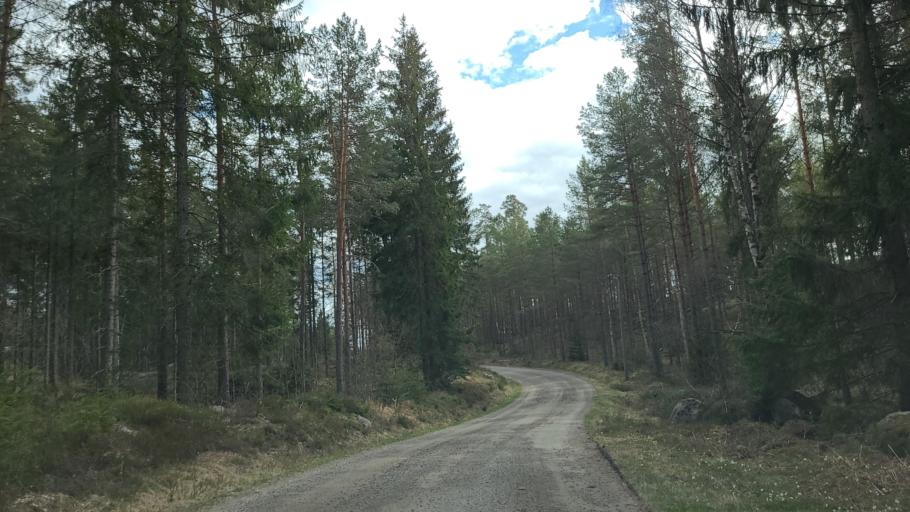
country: SE
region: OEstergoetland
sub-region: Norrkopings Kommun
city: Krokek
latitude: 58.6833
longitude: 16.4232
